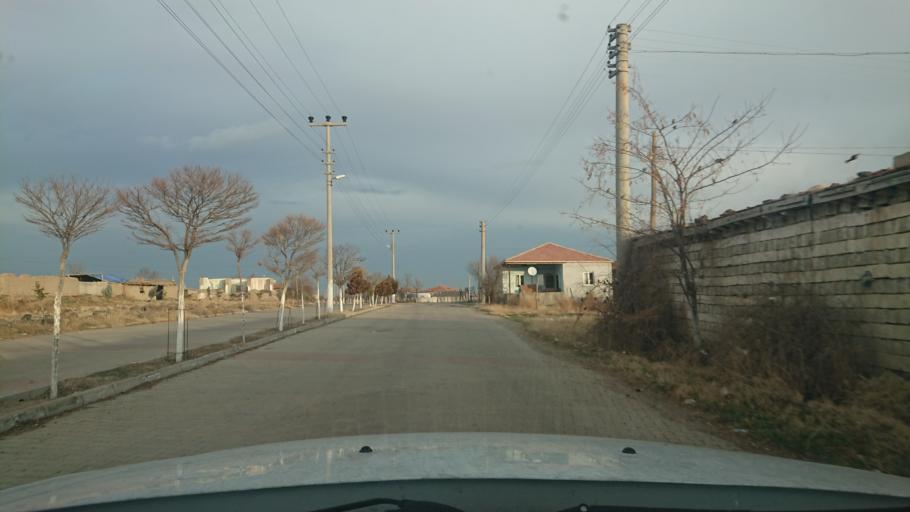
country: TR
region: Aksaray
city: Yesilova
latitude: 38.4138
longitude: 33.8382
